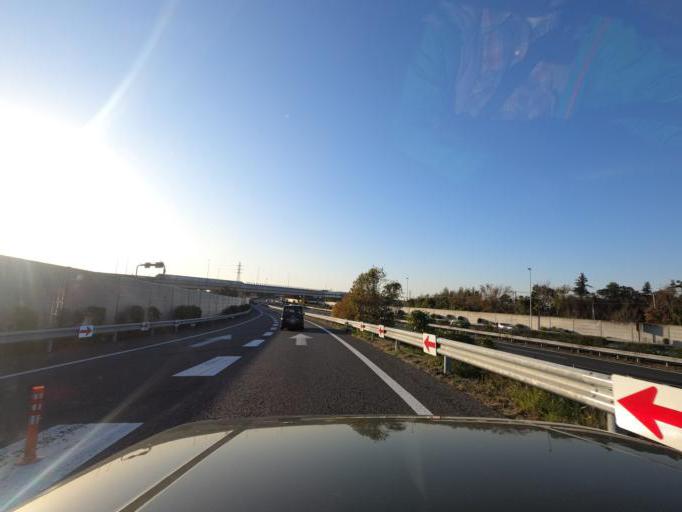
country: JP
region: Ibaraki
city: Naka
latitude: 36.0338
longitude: 140.1256
